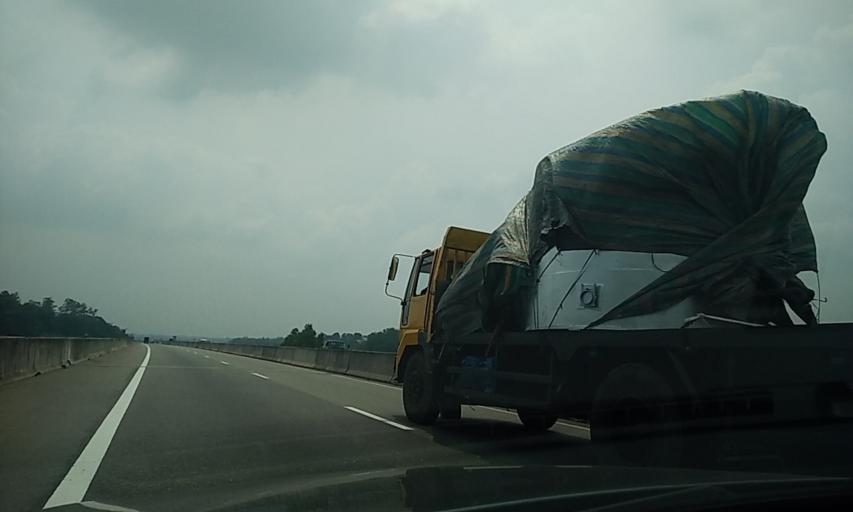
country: LK
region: Western
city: Mulleriyawa
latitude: 6.9029
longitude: 79.9797
